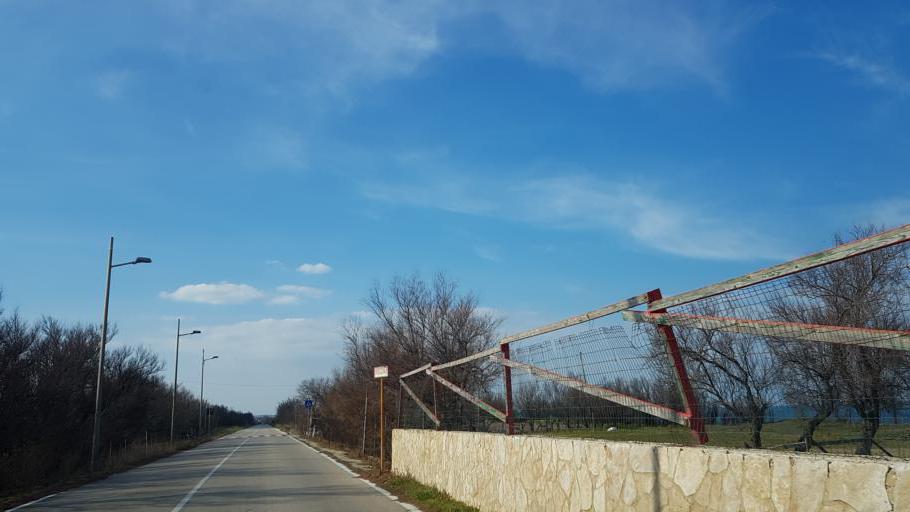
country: IT
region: Apulia
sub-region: Provincia di Brindisi
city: Brindisi
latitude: 40.6890
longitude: 17.8453
